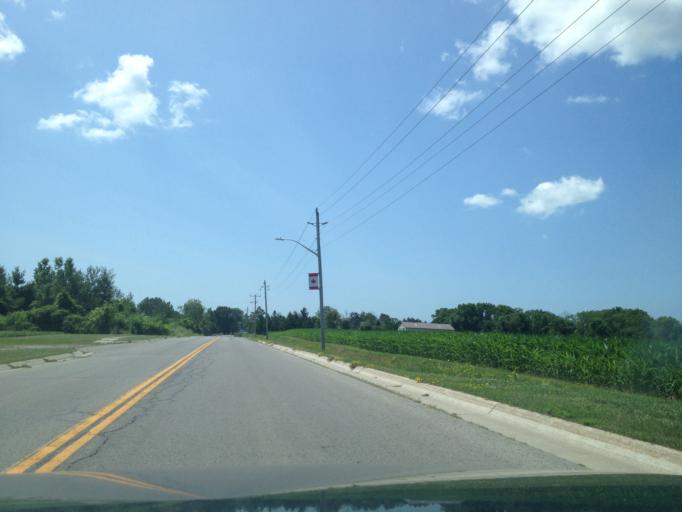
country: CA
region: Ontario
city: Norfolk County
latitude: 42.6177
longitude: -80.4583
